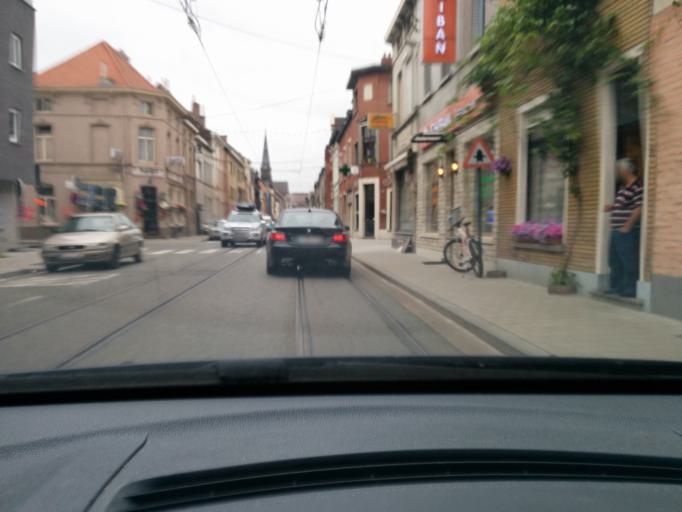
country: BE
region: Flanders
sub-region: Provincie Oost-Vlaanderen
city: Ledeberg
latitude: 51.0379
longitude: 3.7477
